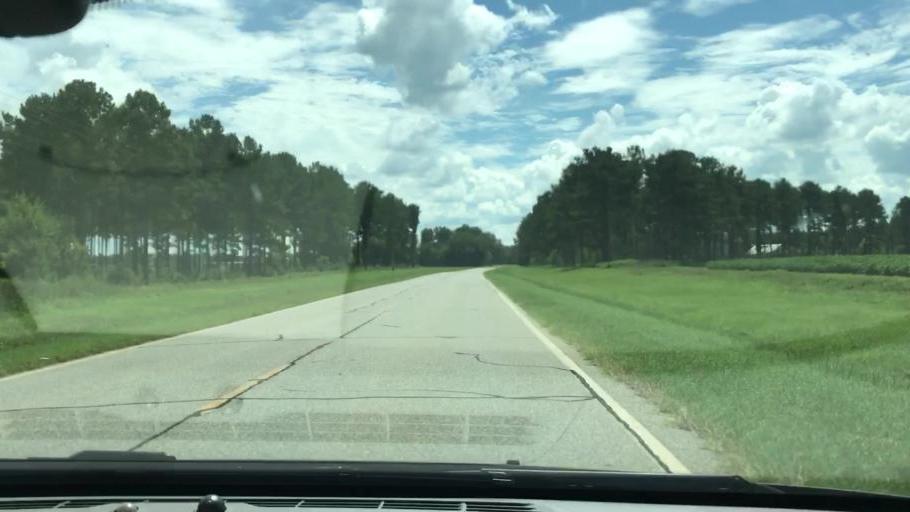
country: US
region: Georgia
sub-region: Quitman County
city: Georgetown
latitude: 32.0532
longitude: -85.0363
